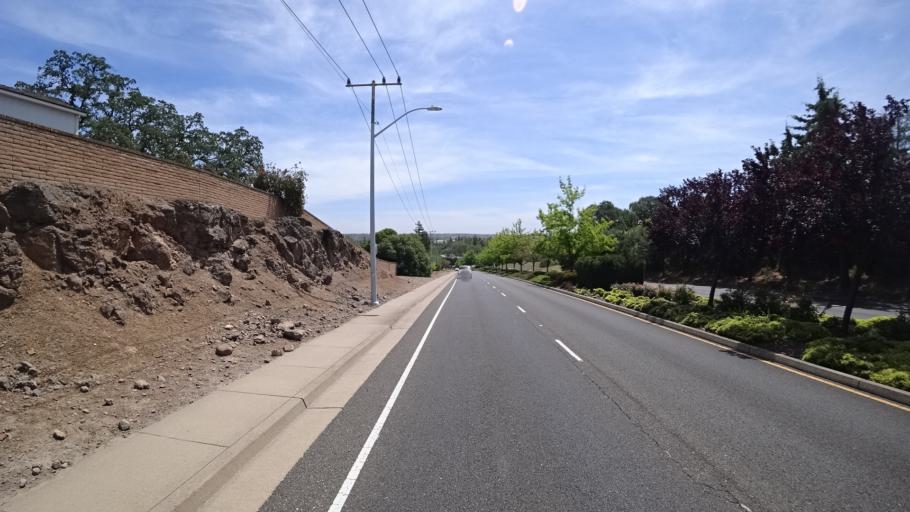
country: US
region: California
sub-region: Placer County
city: Rocklin
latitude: 38.7889
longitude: -121.2557
